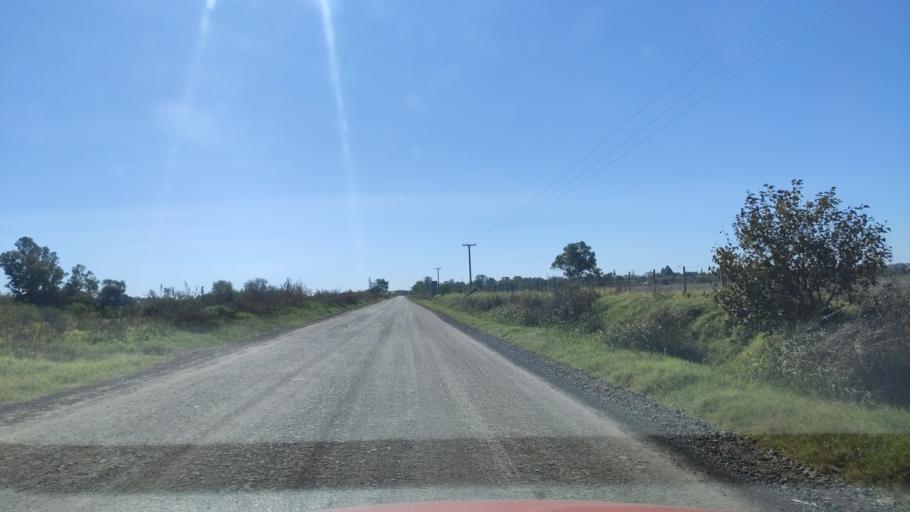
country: AR
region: Cordoba
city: Leones
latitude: -32.6687
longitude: -62.3123
